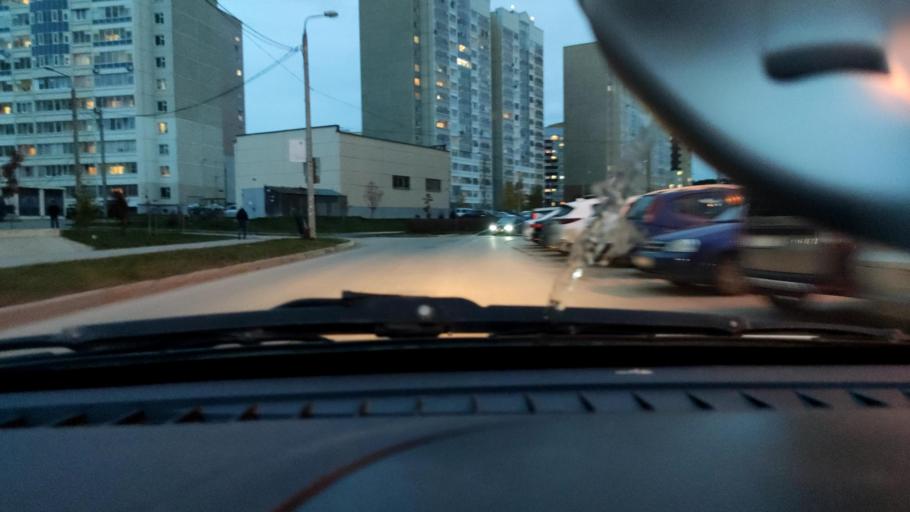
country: RU
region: Perm
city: Kondratovo
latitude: 58.0334
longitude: 56.1401
